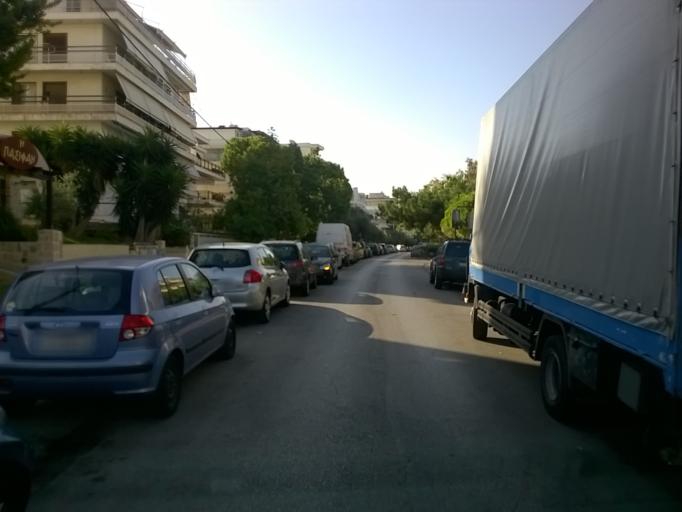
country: GR
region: Attica
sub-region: Nomarchia Athinas
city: Glyfada
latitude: 37.8578
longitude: 23.7534
